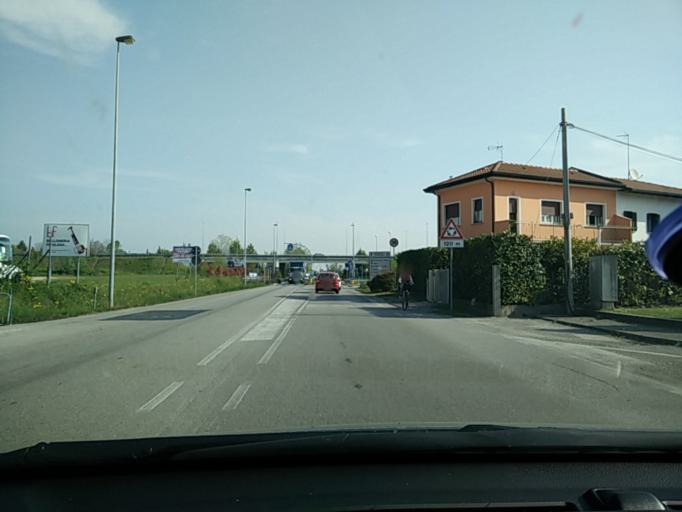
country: IT
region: Friuli Venezia Giulia
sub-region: Provincia di Pordenone
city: Pordenone
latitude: 45.9413
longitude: 12.6519
